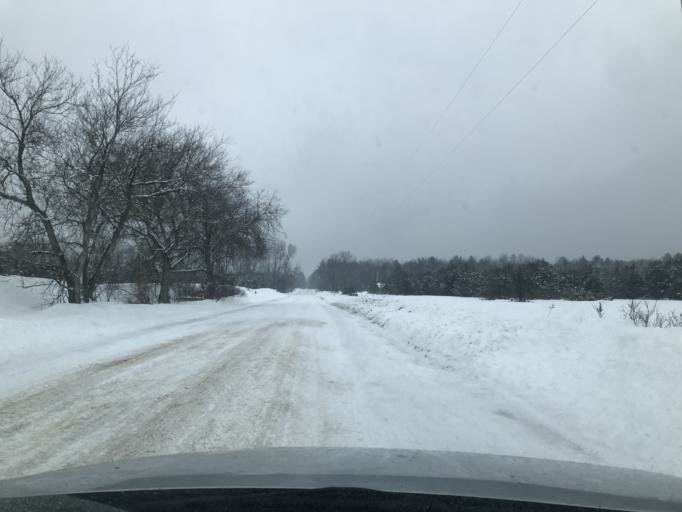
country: US
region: Wisconsin
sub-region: Marinette County
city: Peshtigo
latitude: 45.3812
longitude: -87.9293
